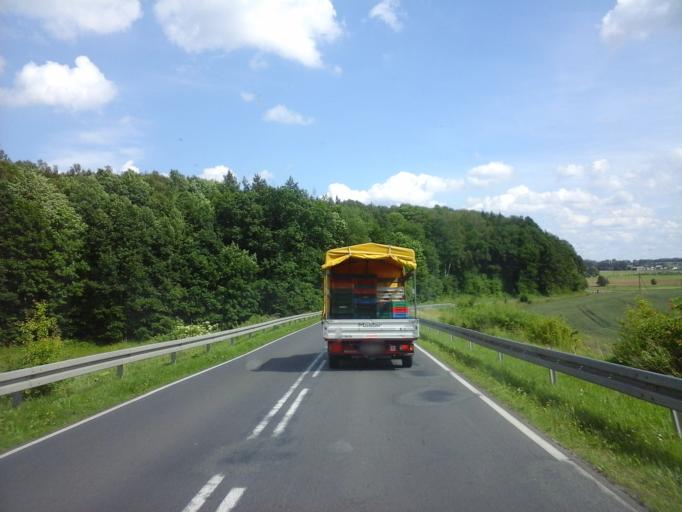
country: PL
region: West Pomeranian Voivodeship
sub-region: Powiat swidwinski
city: Swidwin
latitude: 53.8073
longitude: 15.7670
